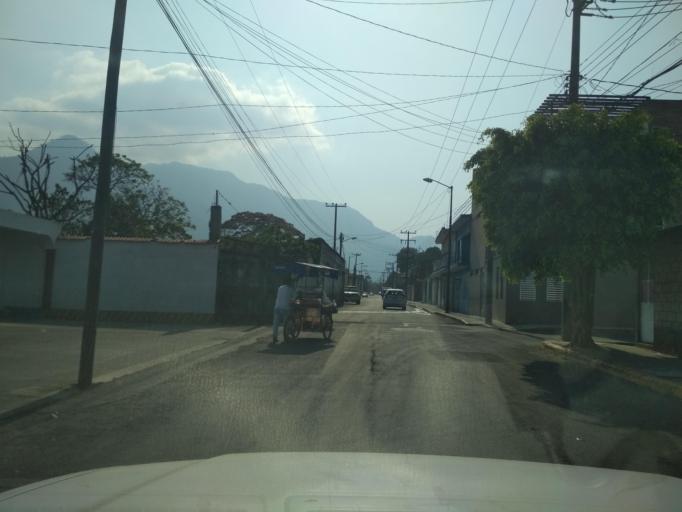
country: MX
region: Veracruz
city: Jalapilla
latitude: 18.8379
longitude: -97.0880
